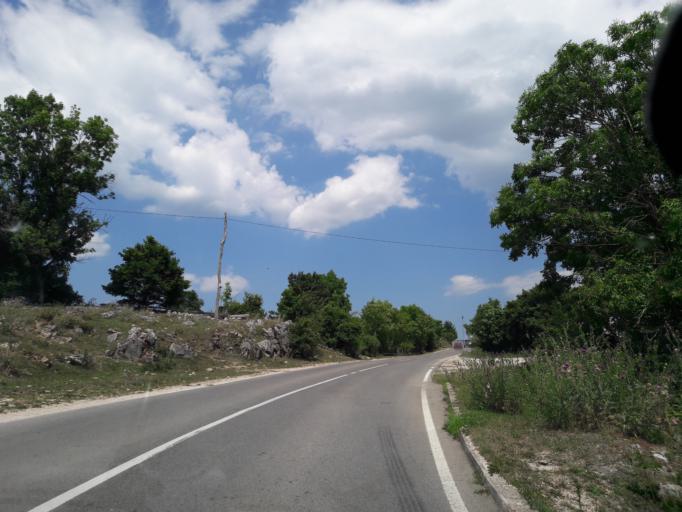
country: BA
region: Republika Srpska
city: Sipovo
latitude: 44.1543
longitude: 17.1678
